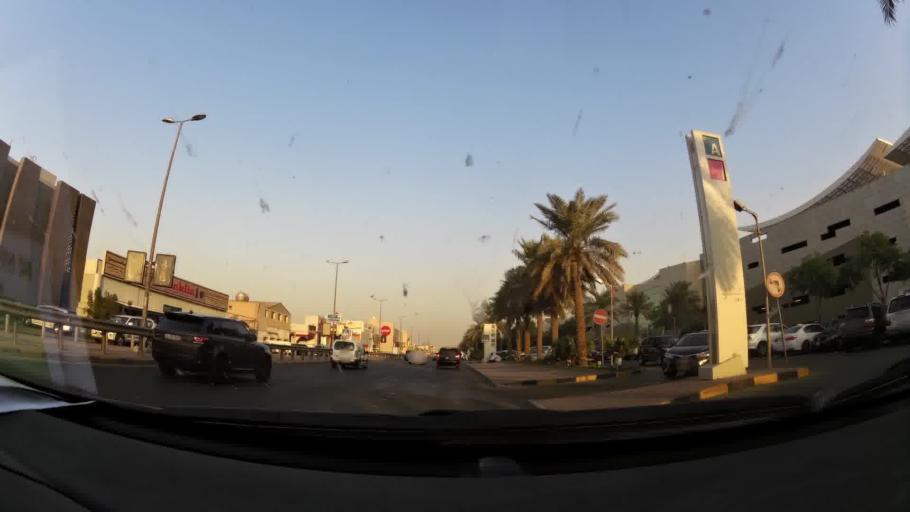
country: KW
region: Al Asimah
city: Ar Rabiyah
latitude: 29.3036
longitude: 47.9299
